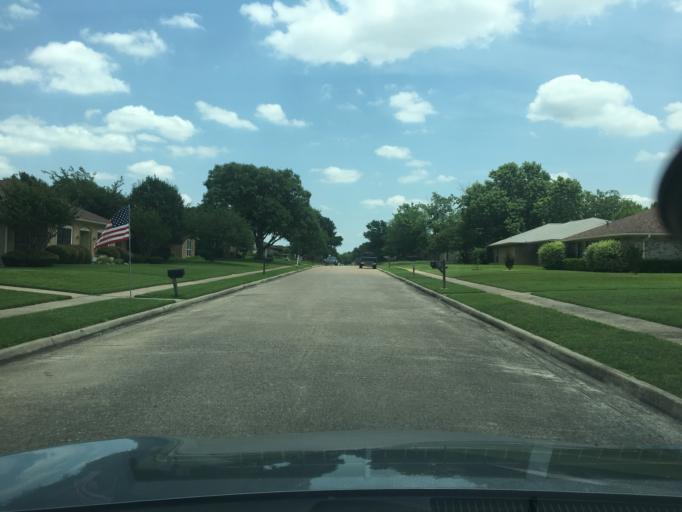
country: US
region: Texas
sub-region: Dallas County
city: Richardson
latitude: 32.9574
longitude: -96.6893
